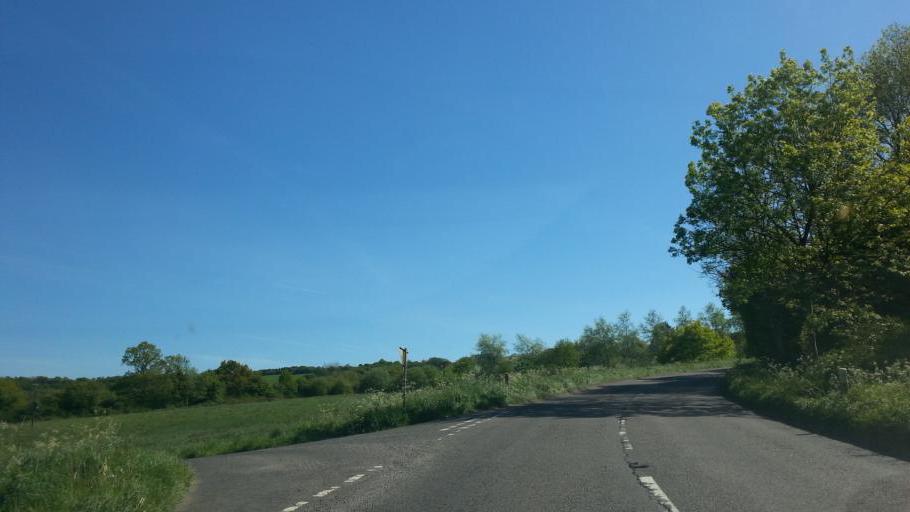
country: GB
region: England
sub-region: Dorset
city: Shaftesbury
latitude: 51.0372
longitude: -2.1847
